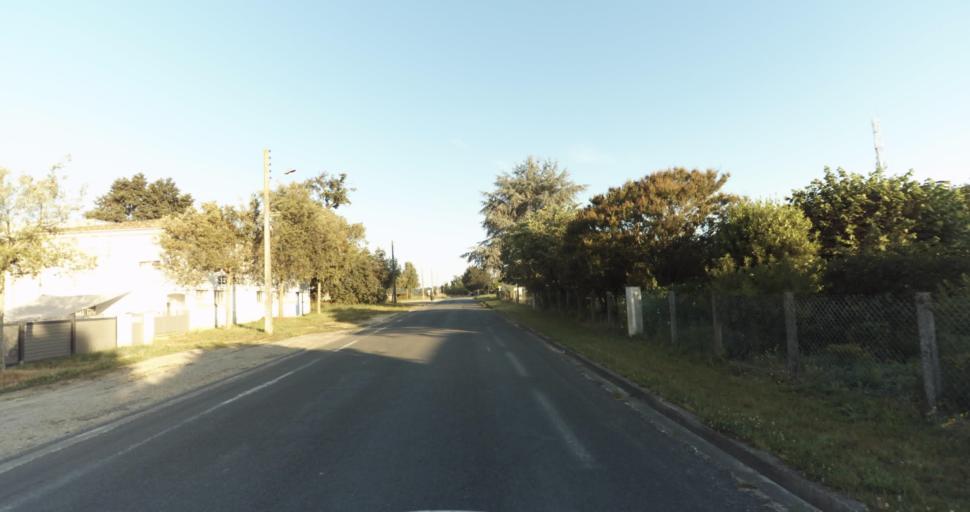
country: FR
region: Aquitaine
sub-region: Departement de la Gironde
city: Bazas
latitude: 44.4342
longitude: -0.2279
